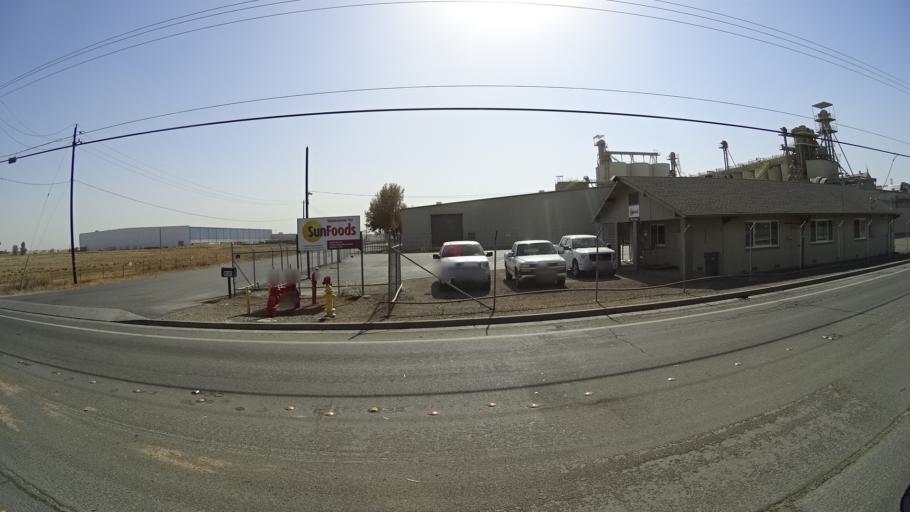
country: US
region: California
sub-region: Yolo County
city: Woodland
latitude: 38.6920
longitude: -121.7433
